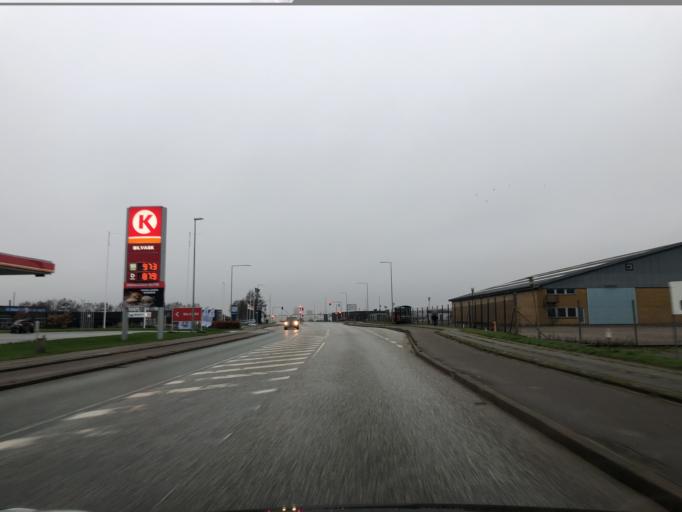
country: DK
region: Central Jutland
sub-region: Herning Kommune
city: Lind
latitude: 56.1079
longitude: 8.9790
